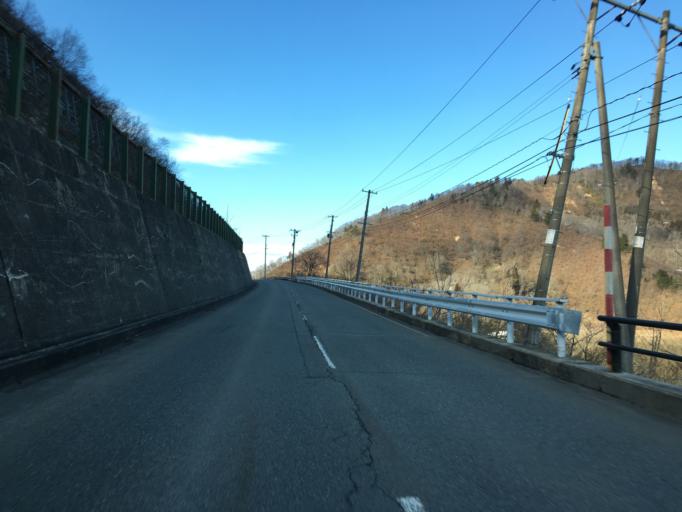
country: JP
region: Yamagata
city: Nagai
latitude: 37.9574
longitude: 139.9169
